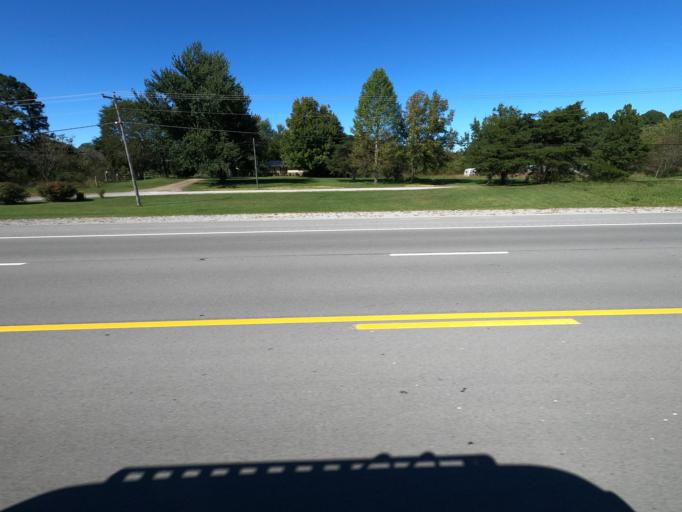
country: US
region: Tennessee
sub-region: Maury County
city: Mount Pleasant
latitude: 35.4464
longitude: -87.2731
